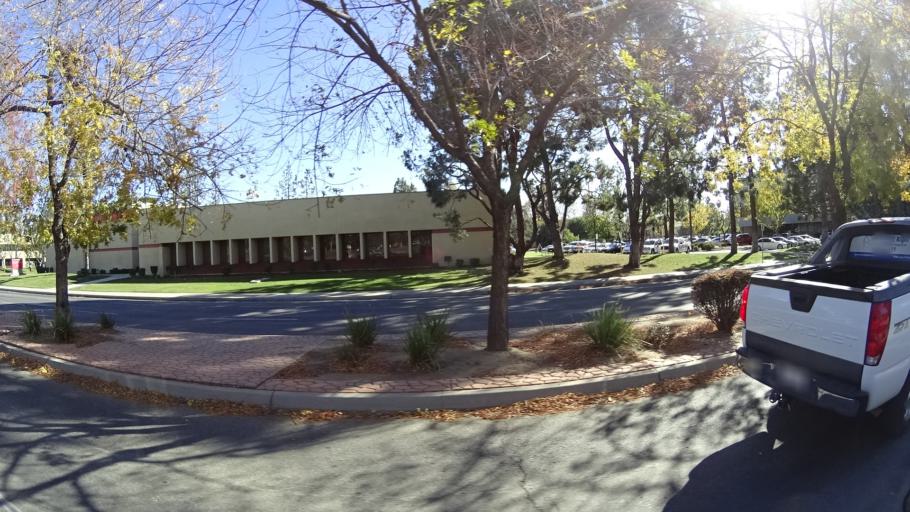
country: US
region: California
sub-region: Kern County
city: Bakersfield
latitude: 35.3622
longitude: -119.0593
